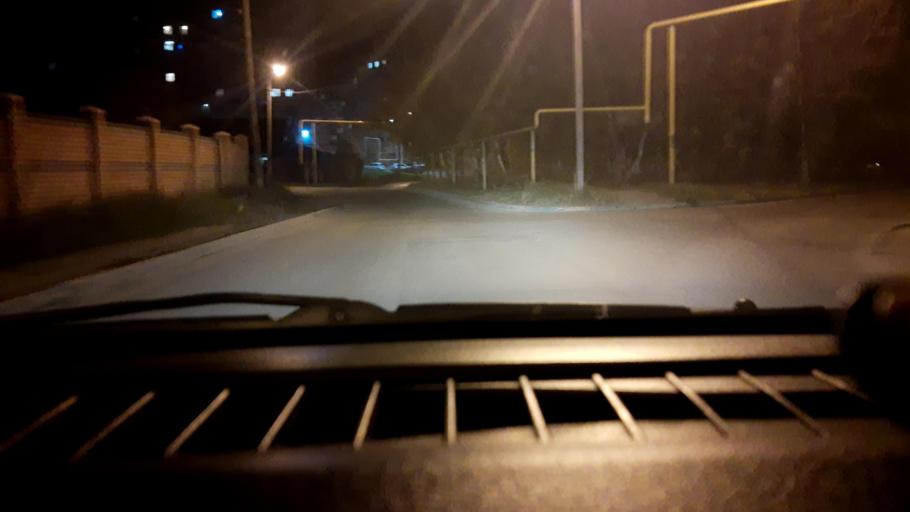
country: RU
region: Nizjnij Novgorod
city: Gorbatovka
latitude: 56.3793
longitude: 43.7992
